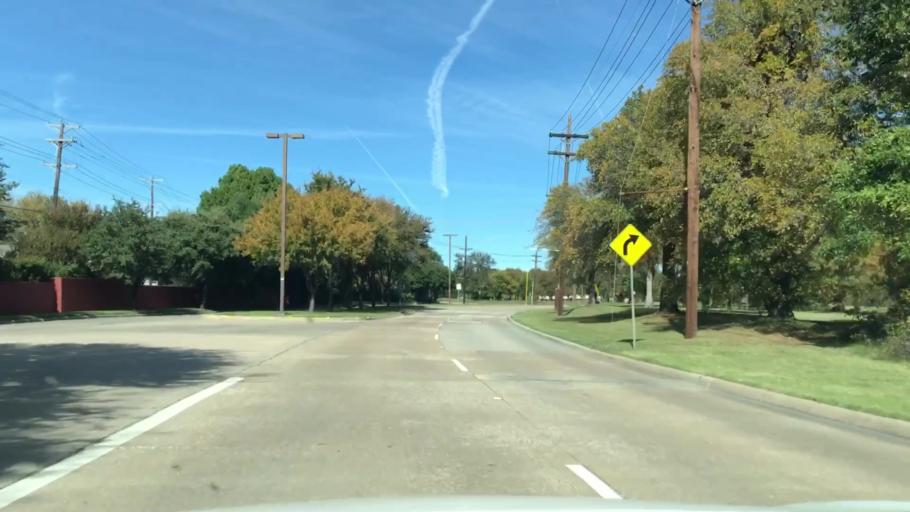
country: US
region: Texas
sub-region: Dallas County
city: Addison
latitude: 33.0175
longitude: -96.8572
